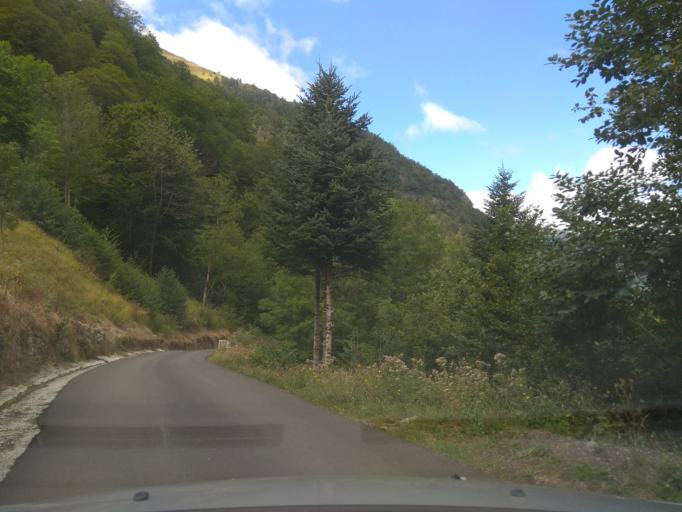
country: ES
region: Catalonia
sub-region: Provincia de Lleida
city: Vielha
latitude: 42.7026
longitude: 0.7120
